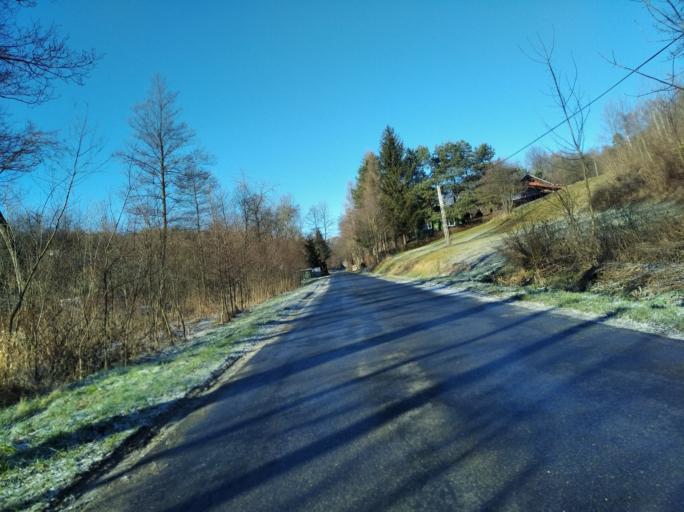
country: PL
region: Subcarpathian Voivodeship
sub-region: Powiat strzyzowski
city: Czudec
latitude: 49.9513
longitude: 21.7759
